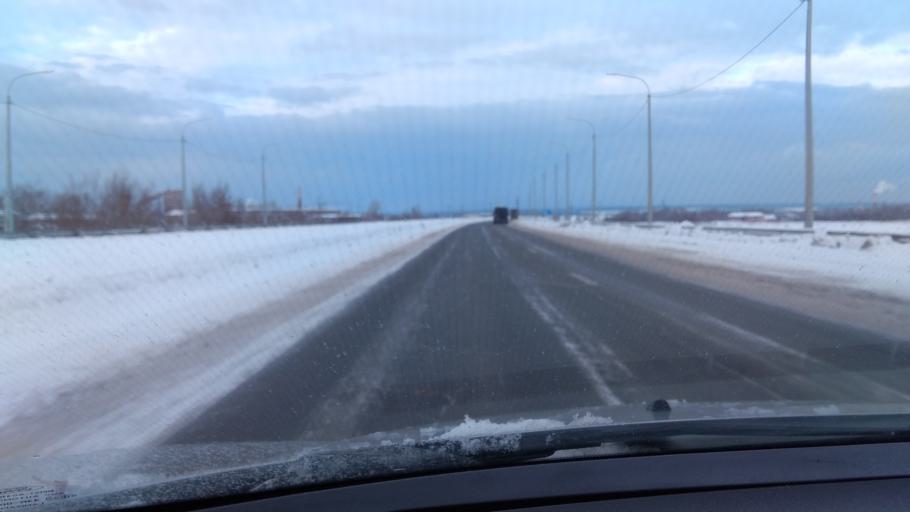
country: RU
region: Sverdlovsk
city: Tsementnyy
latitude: 57.4687
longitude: 60.1834
